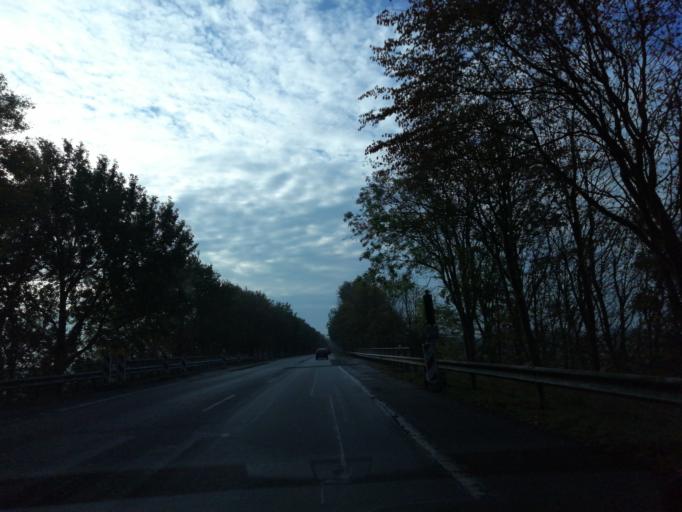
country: DE
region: Lower Saxony
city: Fedderwarden
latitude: 53.5874
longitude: 8.0558
